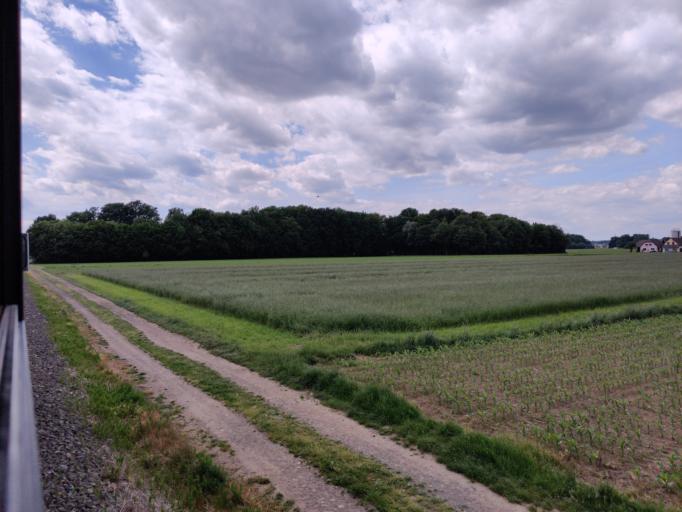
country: AT
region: Styria
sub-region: Politischer Bezirk Suedoststeiermark
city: Eichfeld
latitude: 46.7145
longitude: 15.7349
